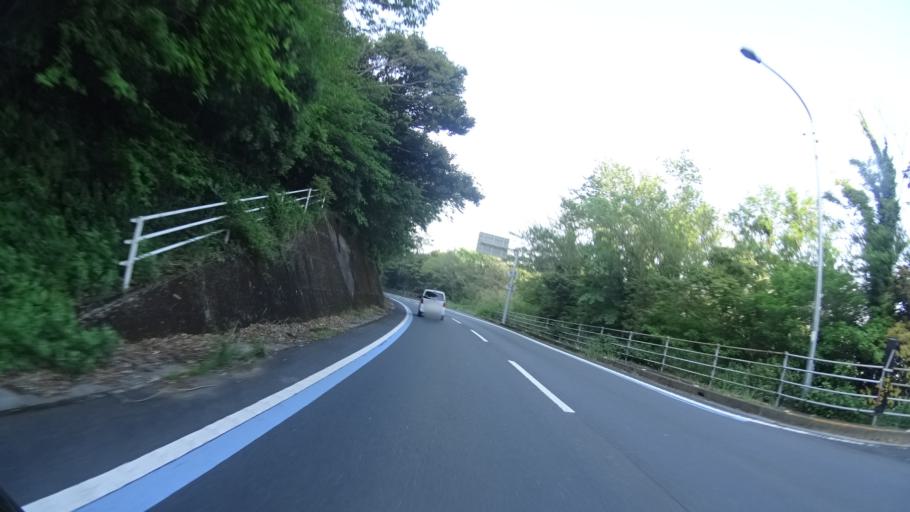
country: JP
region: Ehime
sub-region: Nishiuwa-gun
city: Ikata-cho
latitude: 33.4151
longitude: 132.1732
